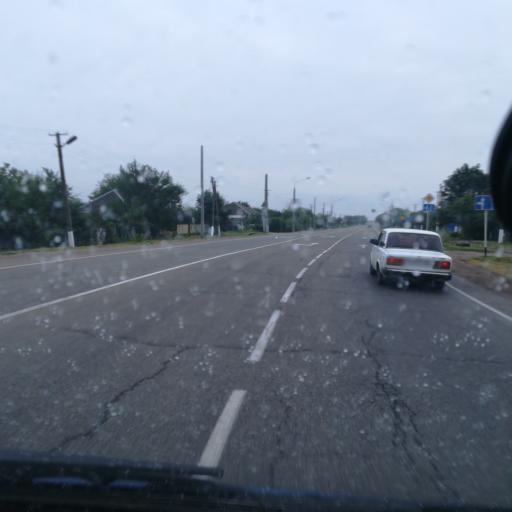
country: RU
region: Krasnodarskiy
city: Krymsk
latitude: 44.9915
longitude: 37.9501
